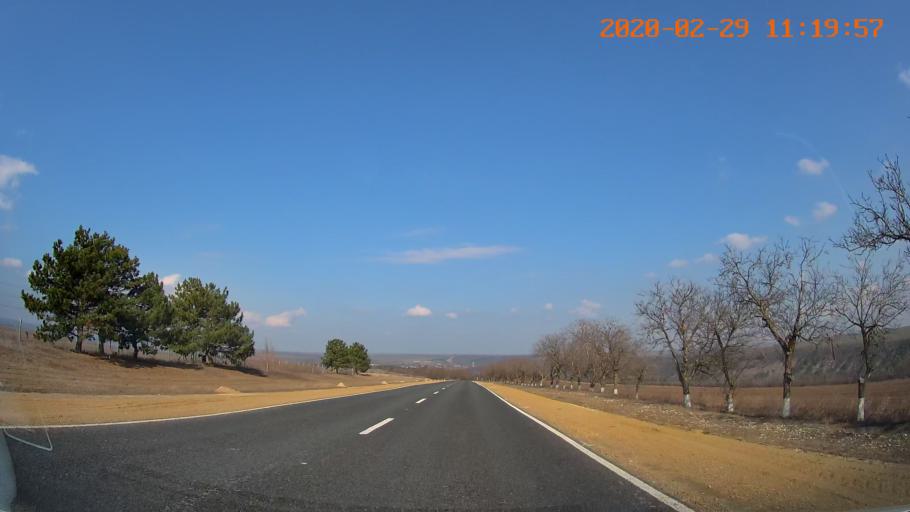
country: MD
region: Telenesti
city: Cocieri
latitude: 47.3579
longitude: 29.1728
